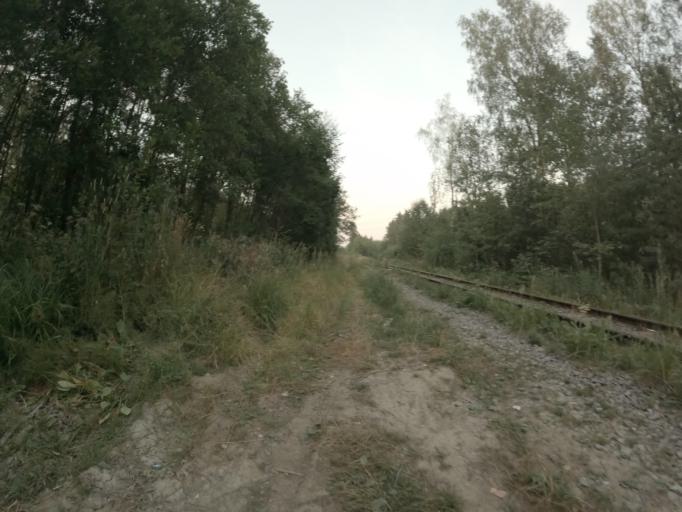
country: RU
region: St.-Petersburg
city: Krasnogvargeisky
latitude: 59.9436
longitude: 30.5260
